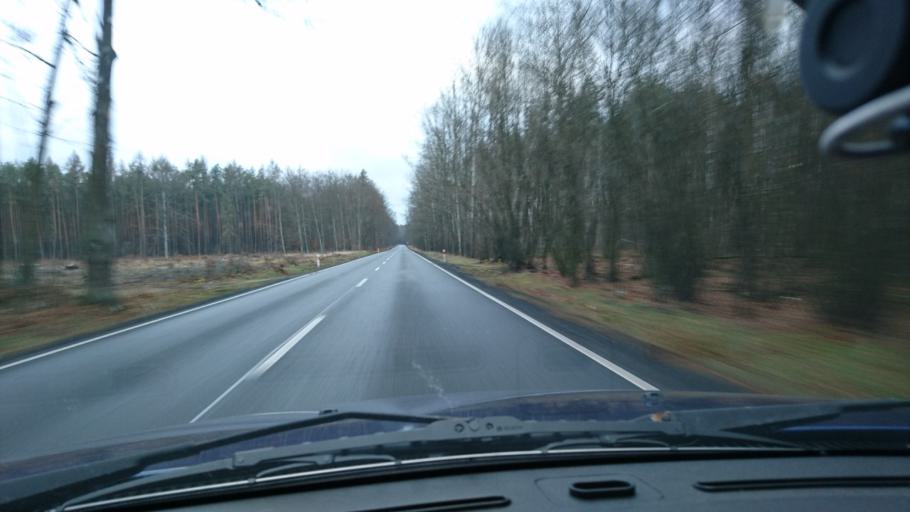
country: PL
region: Opole Voivodeship
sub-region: Powiat oleski
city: Olesno
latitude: 50.9308
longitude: 18.3336
